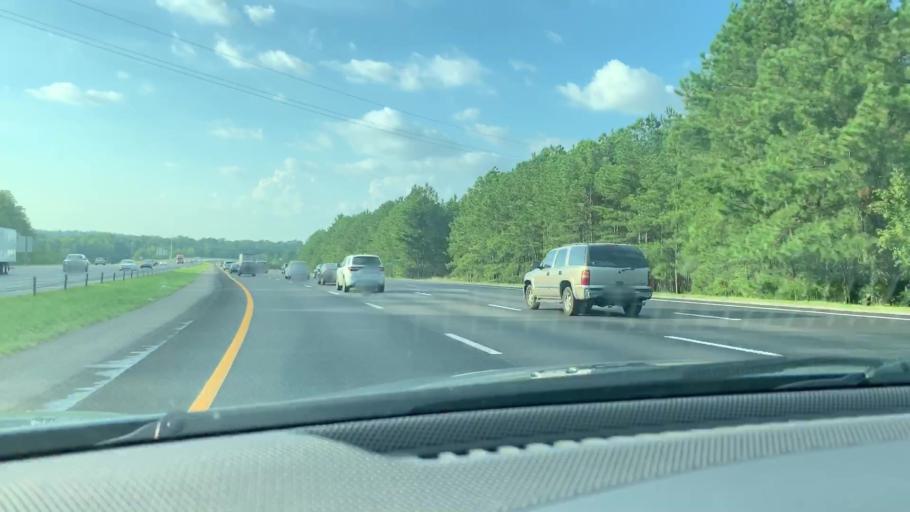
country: US
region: South Carolina
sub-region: Richland County
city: Forest Acres
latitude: 33.9912
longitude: -80.9542
